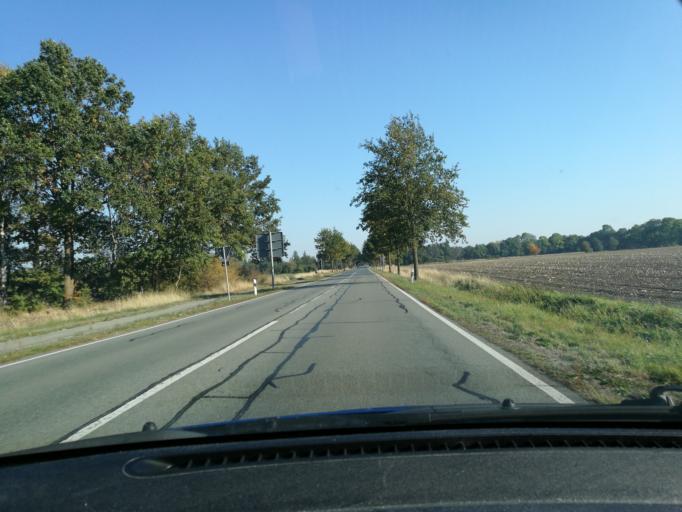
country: DE
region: Lower Saxony
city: Dannenberg
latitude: 53.1008
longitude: 11.0598
